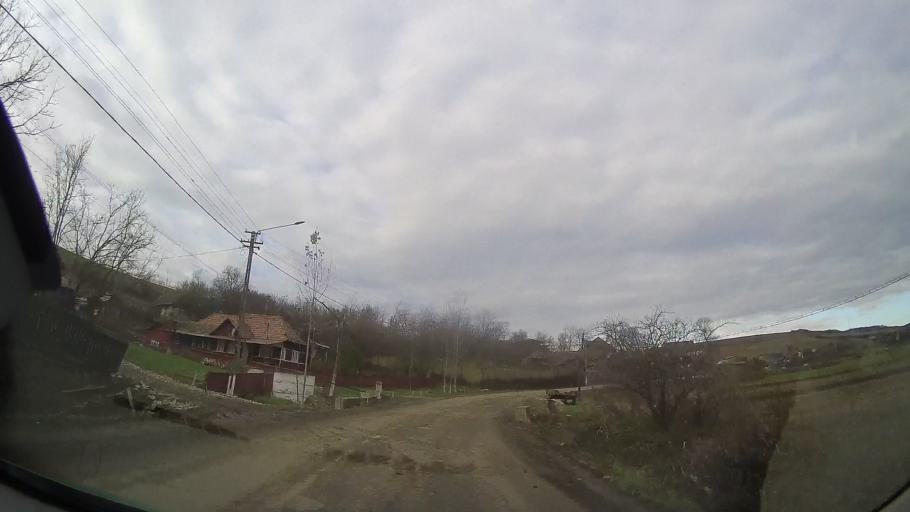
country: RO
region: Bistrita-Nasaud
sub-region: Comuna Micestii de Campie
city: Micestii de Campie
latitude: 46.8328
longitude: 24.3032
